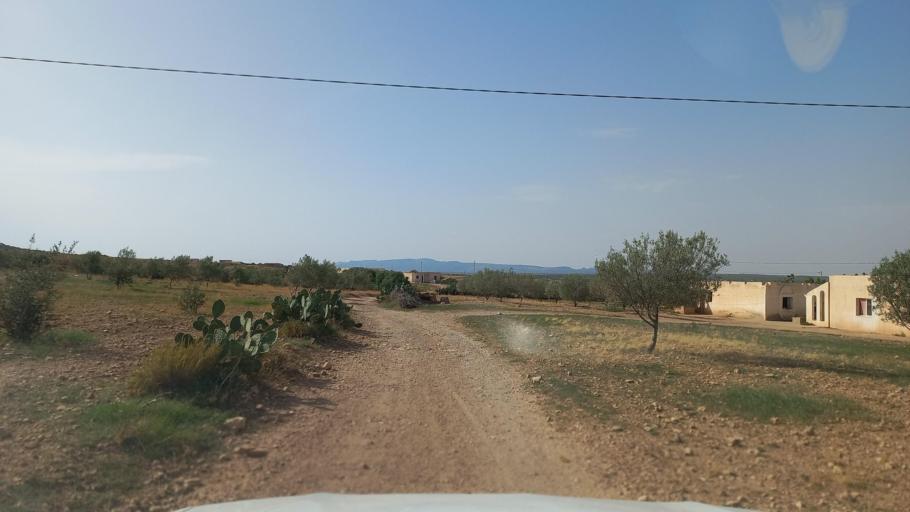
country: TN
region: Al Qasrayn
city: Kasserine
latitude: 35.3384
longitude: 8.8215
